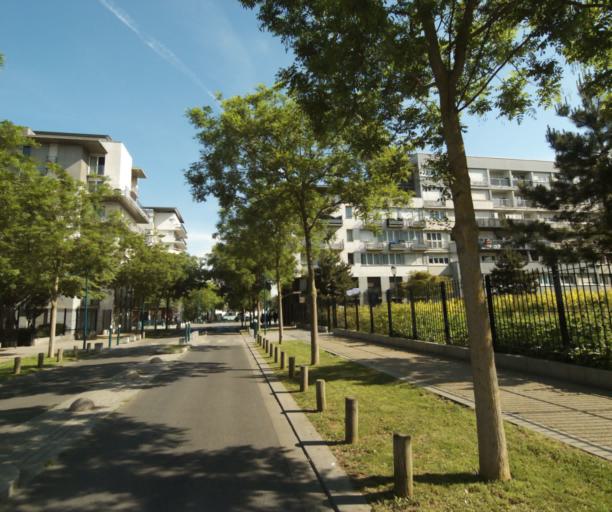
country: FR
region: Ile-de-France
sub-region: Departement des Hauts-de-Seine
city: Gennevilliers
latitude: 48.9325
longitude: 2.2870
